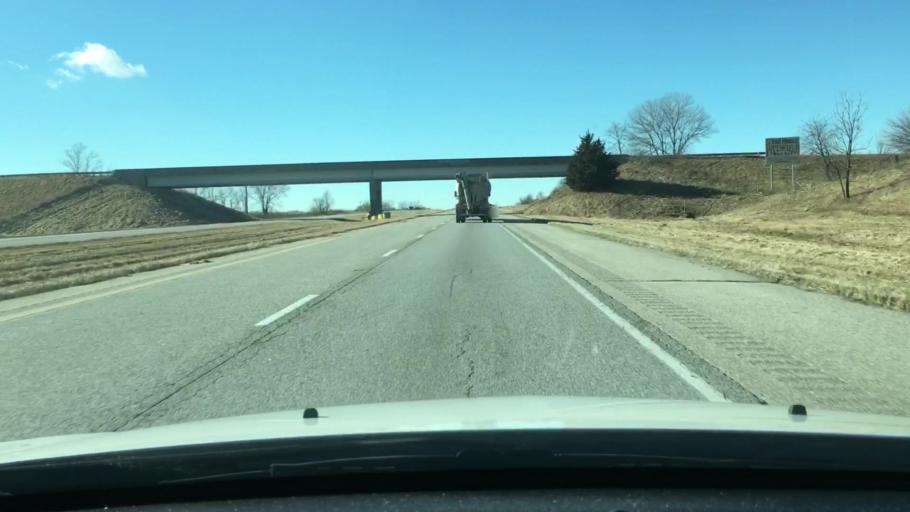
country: US
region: Illinois
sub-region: Pike County
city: Griggsville
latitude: 39.6784
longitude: -90.7025
